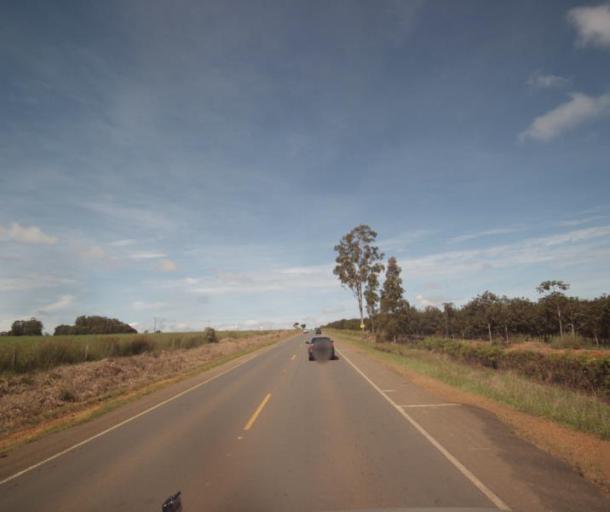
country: BR
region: Goias
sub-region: Anapolis
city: Anapolis
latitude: -16.1908
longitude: -48.9059
